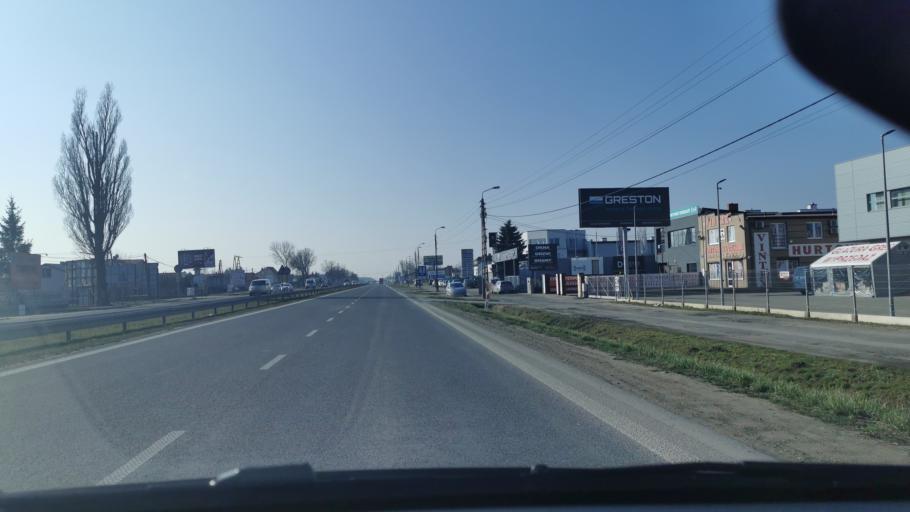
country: PL
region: Masovian Voivodeship
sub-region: Powiat pruszkowski
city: Nowe Grocholice
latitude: 52.1227
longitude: 20.8941
